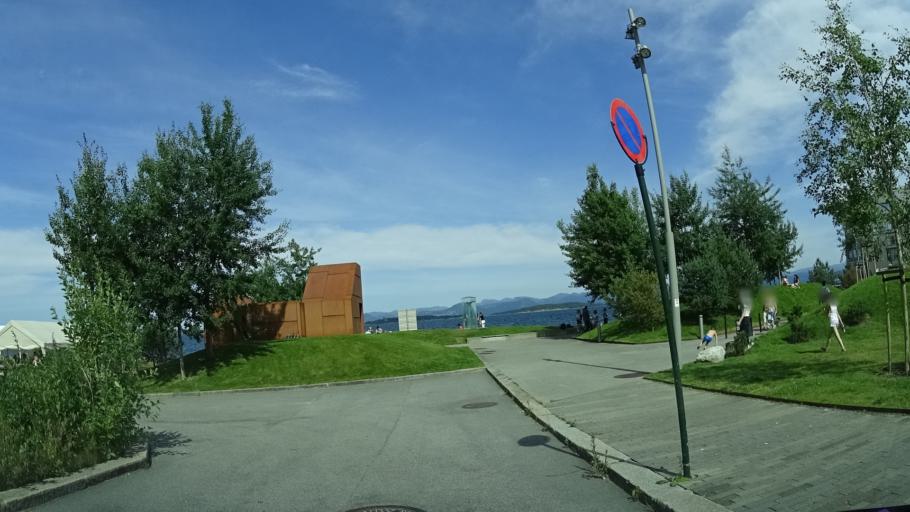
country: NO
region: Rogaland
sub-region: Stavanger
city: Stavanger
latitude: 58.9698
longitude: 5.7585
